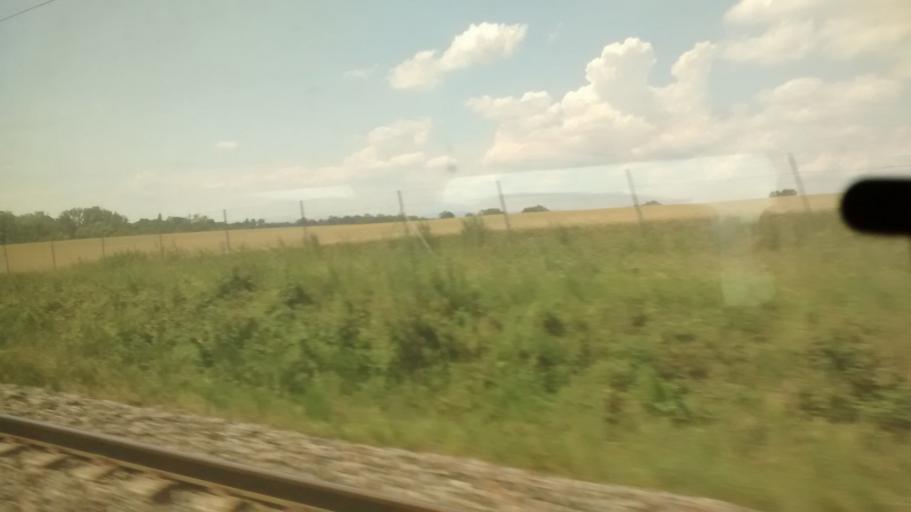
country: FR
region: Rhone-Alpes
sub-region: Departement de l'Ain
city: Grieges
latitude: 46.2111
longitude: 4.8573
